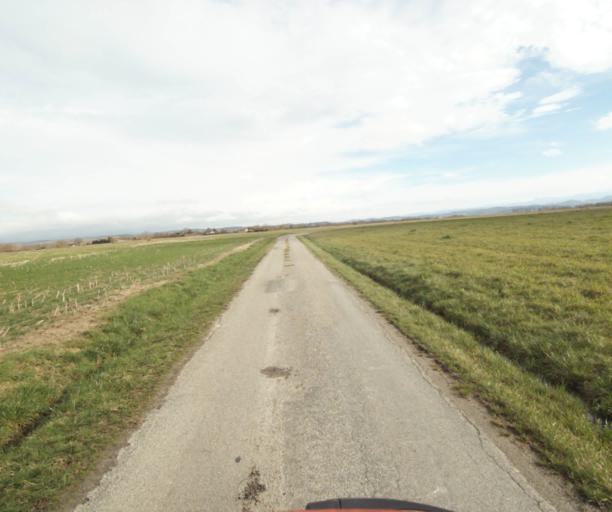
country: FR
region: Midi-Pyrenees
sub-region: Departement de l'Ariege
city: La Tour-du-Crieu
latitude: 43.1188
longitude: 1.7032
